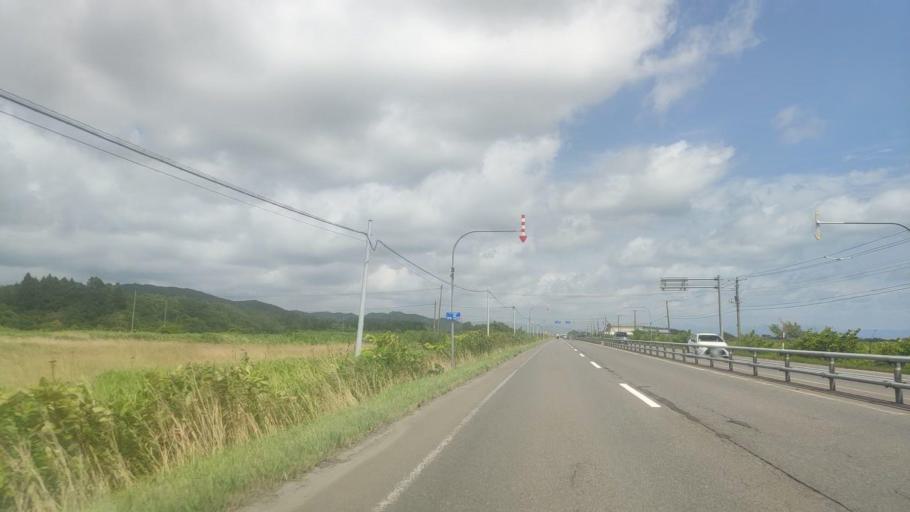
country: JP
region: Hokkaido
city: Niseko Town
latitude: 42.4115
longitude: 140.3073
